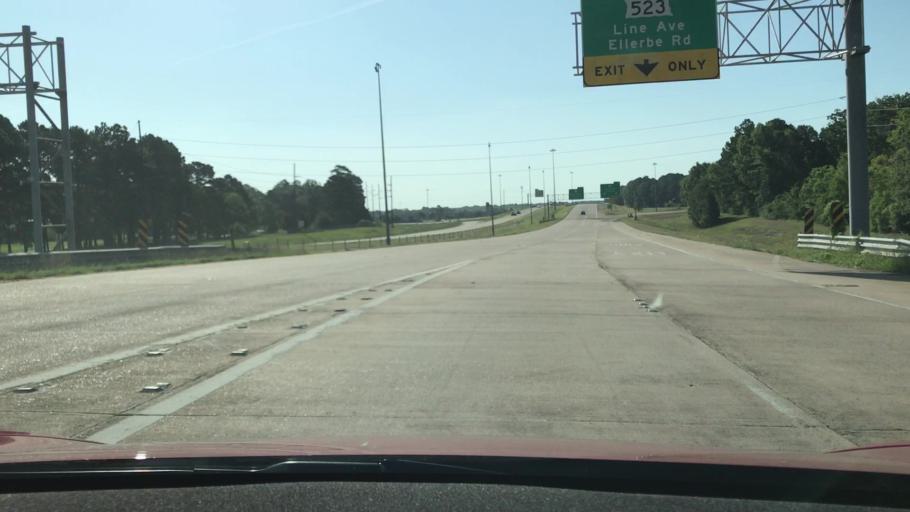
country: US
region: Louisiana
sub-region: Bossier Parish
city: Bossier City
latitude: 32.4179
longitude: -93.7434
